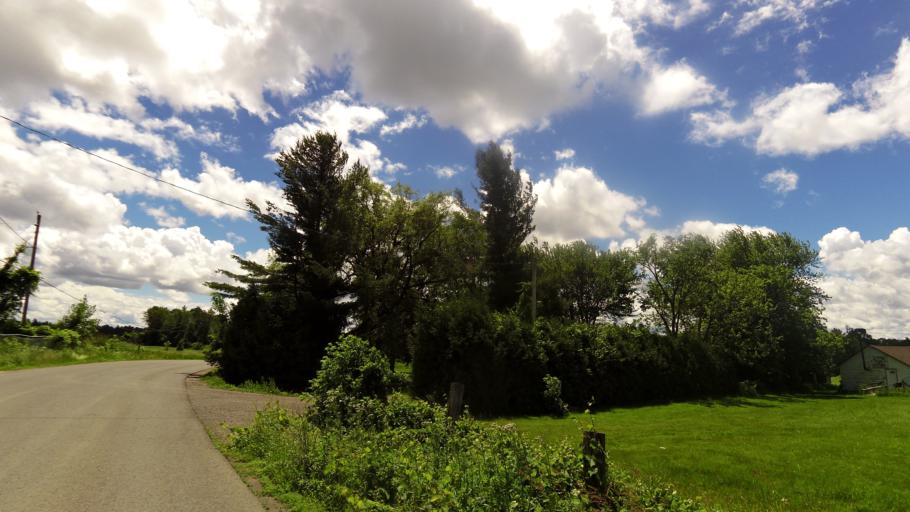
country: CA
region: Quebec
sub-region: Laurentides
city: Oka
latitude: 45.4781
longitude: -74.0992
